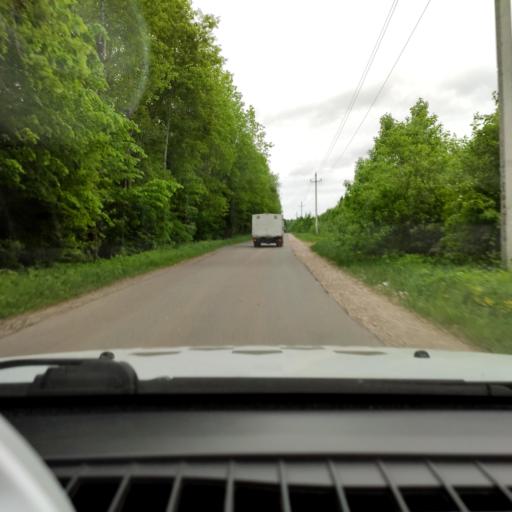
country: RU
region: Perm
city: Novyye Lyady
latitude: 58.0444
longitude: 56.6354
